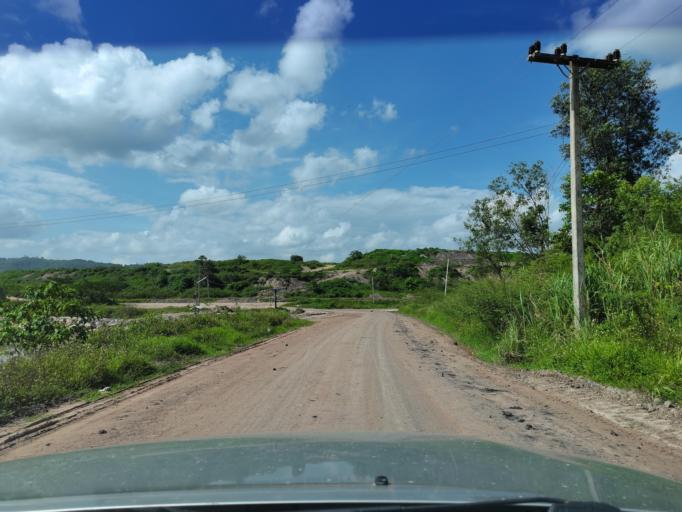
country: LA
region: Loungnamtha
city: Muang Nale
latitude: 20.5868
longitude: 101.0598
